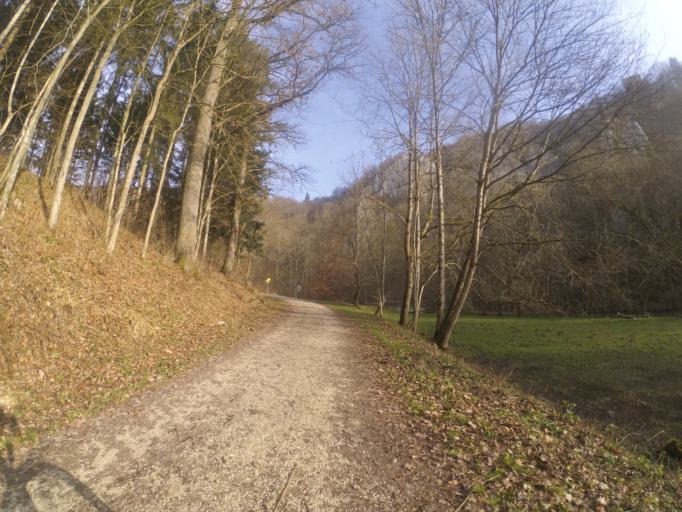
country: DE
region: Baden-Wuerttemberg
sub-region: Tuebingen Region
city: Emeringen
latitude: 48.2738
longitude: 9.5189
